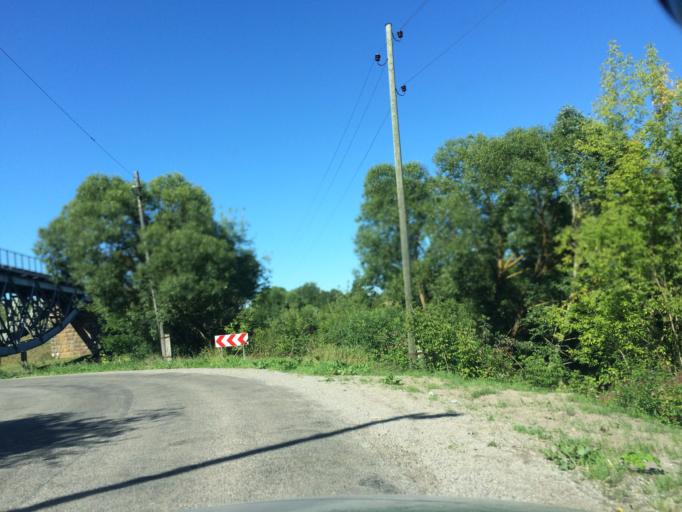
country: LV
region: Rezekne
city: Rezekne
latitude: 56.5071
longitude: 27.3184
